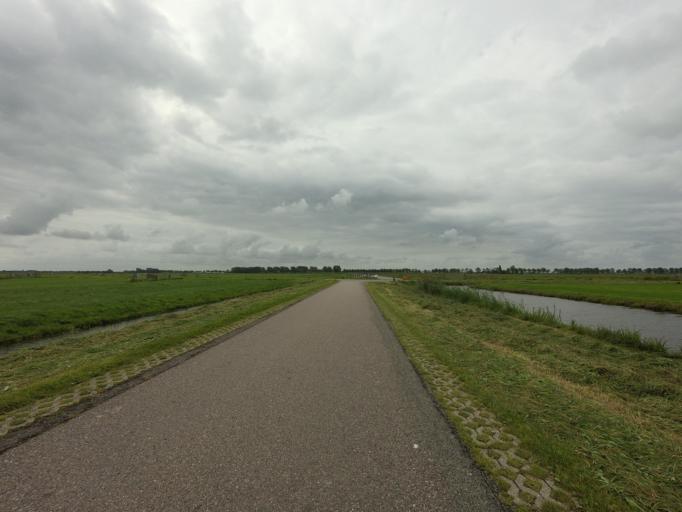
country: NL
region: North Holland
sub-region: Gemeente Edam-Volendam
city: Edam
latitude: 52.5532
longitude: 5.0303
